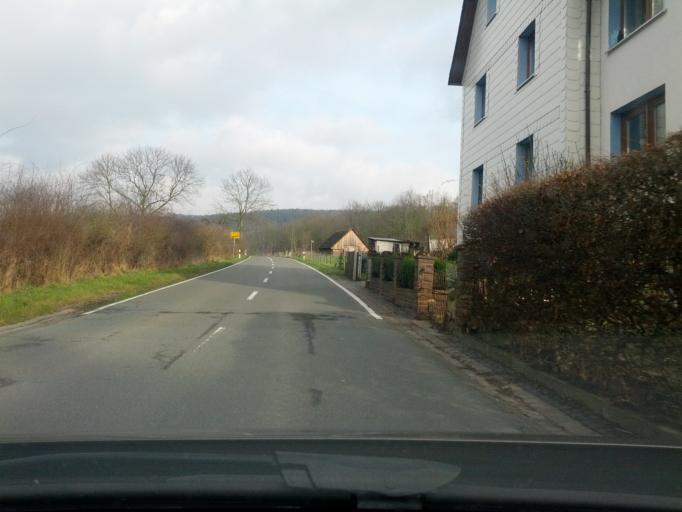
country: DE
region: Lower Saxony
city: Derental
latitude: 51.6913
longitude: 9.4011
